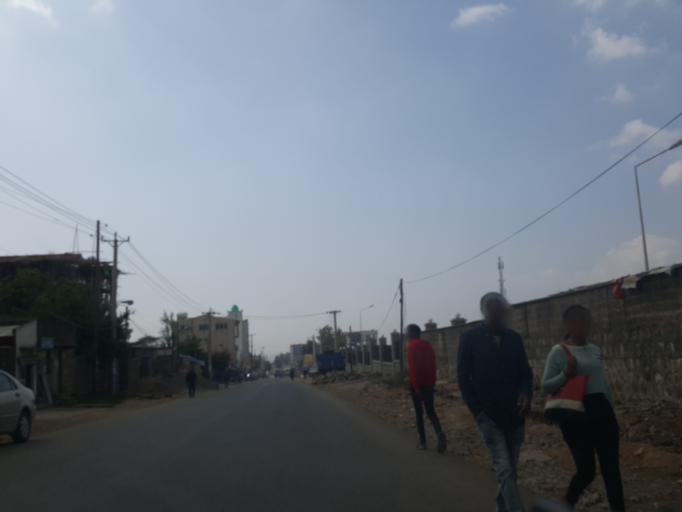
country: ET
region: Adis Abeba
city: Addis Ababa
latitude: 9.0647
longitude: 38.7207
